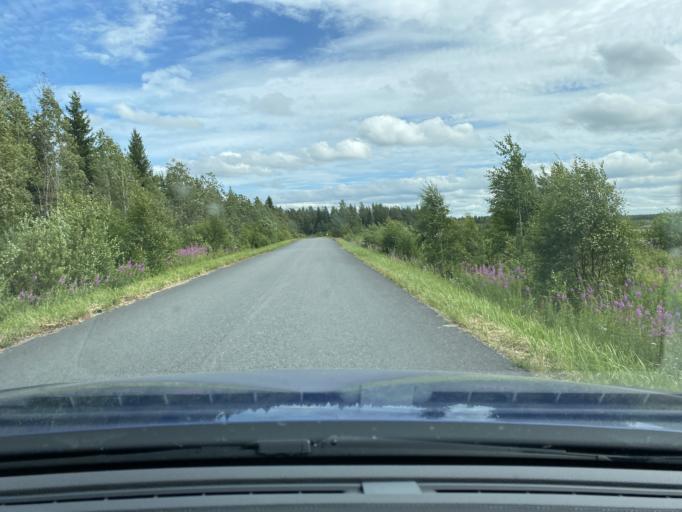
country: FI
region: Southern Ostrobothnia
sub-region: Seinaejoki
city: Jurva
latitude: 62.6267
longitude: 22.0214
